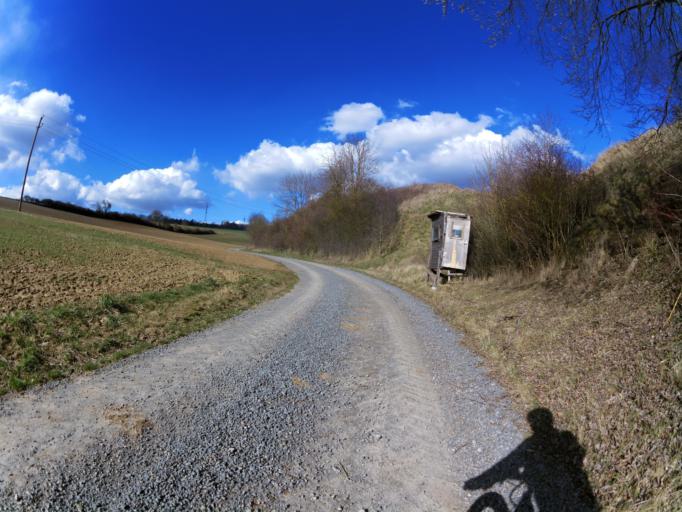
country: DE
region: Bavaria
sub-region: Regierungsbezirk Unterfranken
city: Greussenheim
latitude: 49.8015
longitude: 9.7683
